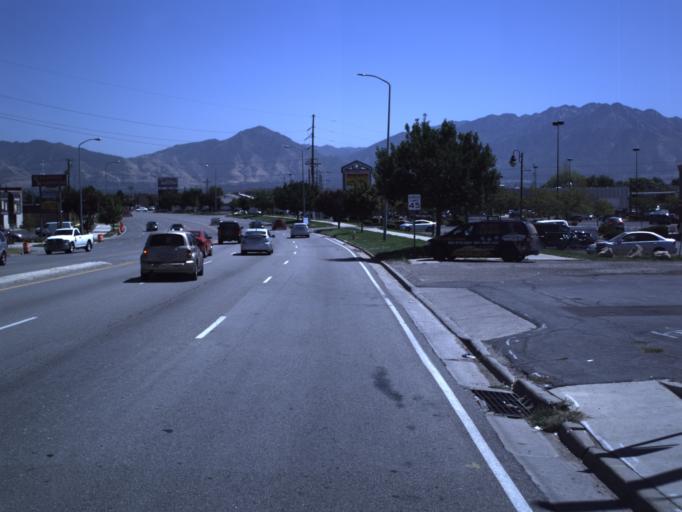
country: US
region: Utah
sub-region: Salt Lake County
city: Taylorsville
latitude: 40.6965
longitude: -111.9379
